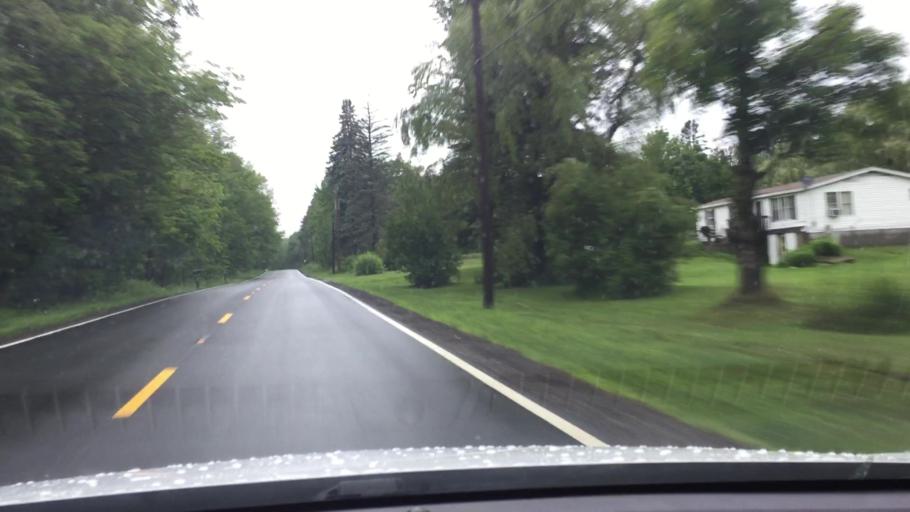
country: US
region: Massachusetts
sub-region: Berkshire County
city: Becket
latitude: 42.3539
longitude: -73.1290
